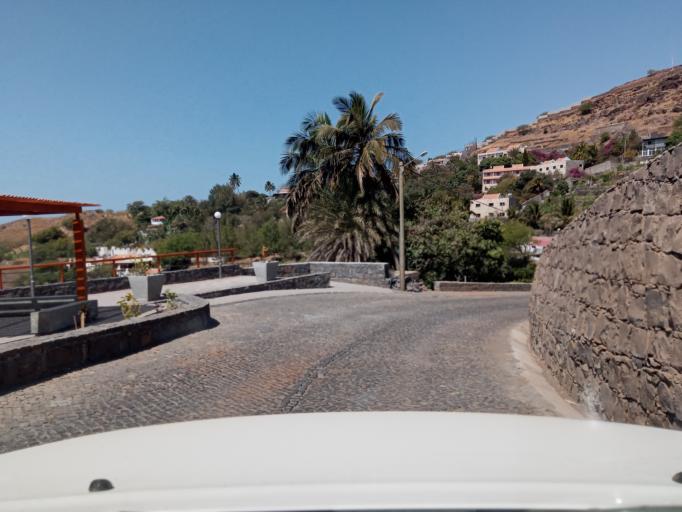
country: CV
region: Ribeira Grande de Santiago
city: Cidade Velha
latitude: 14.9164
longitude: -23.6087
